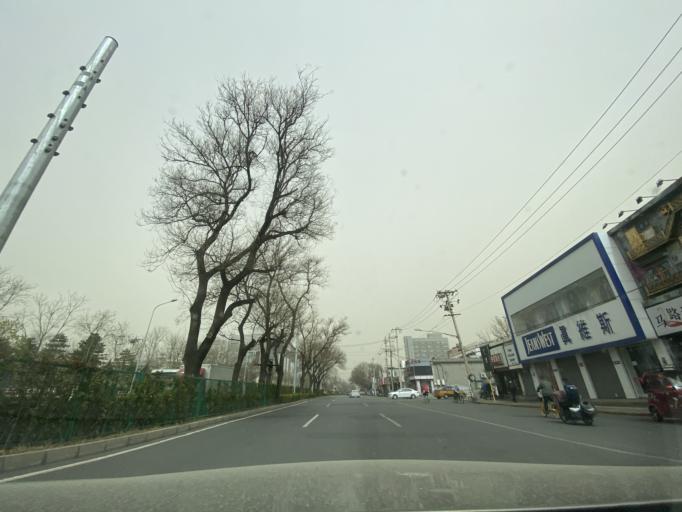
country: CN
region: Beijing
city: Jinrongjie
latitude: 39.9397
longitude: 116.3664
